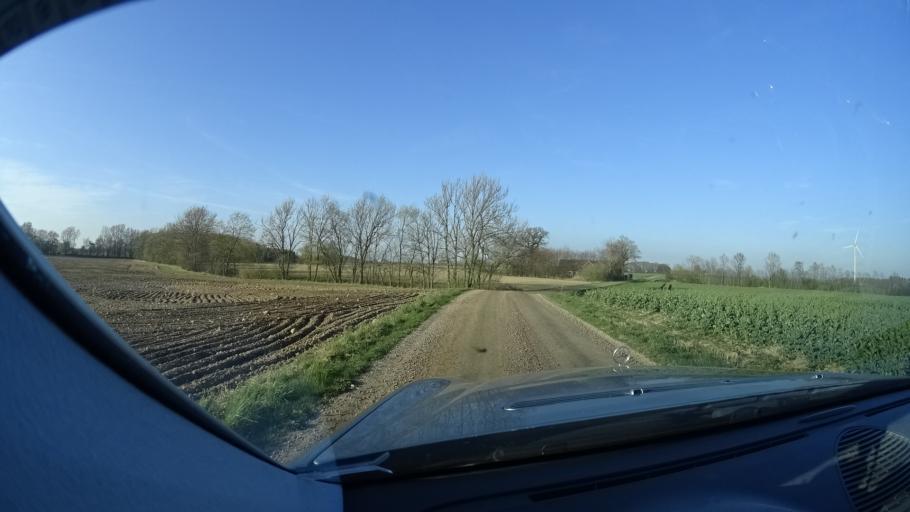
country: SE
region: Skane
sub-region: Hoors Kommun
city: Loberod
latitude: 55.8464
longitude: 13.4628
